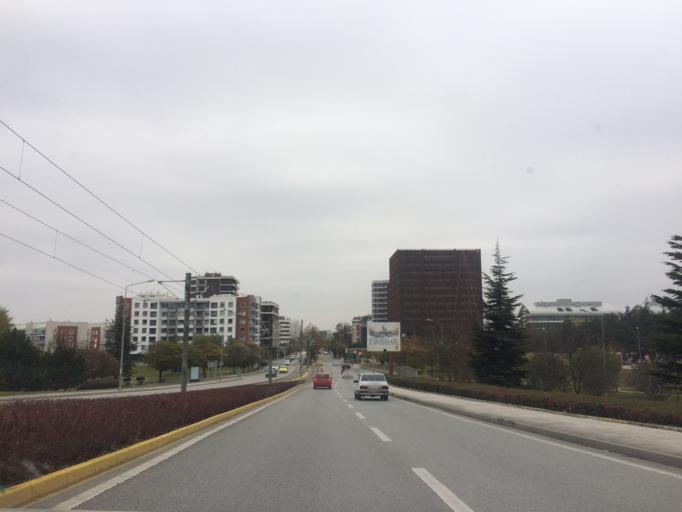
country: TR
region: Eskisehir
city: Eskisehir
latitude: 39.7868
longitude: 30.4973
